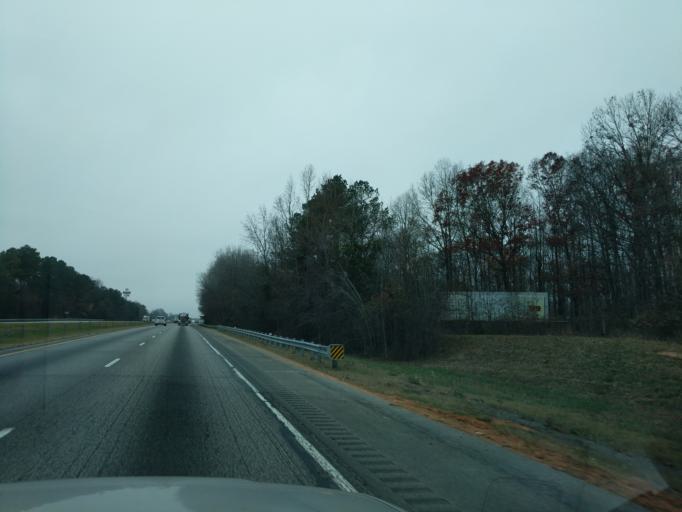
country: US
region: Georgia
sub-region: Franklin County
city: Carnesville
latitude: 34.3972
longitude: -83.2164
